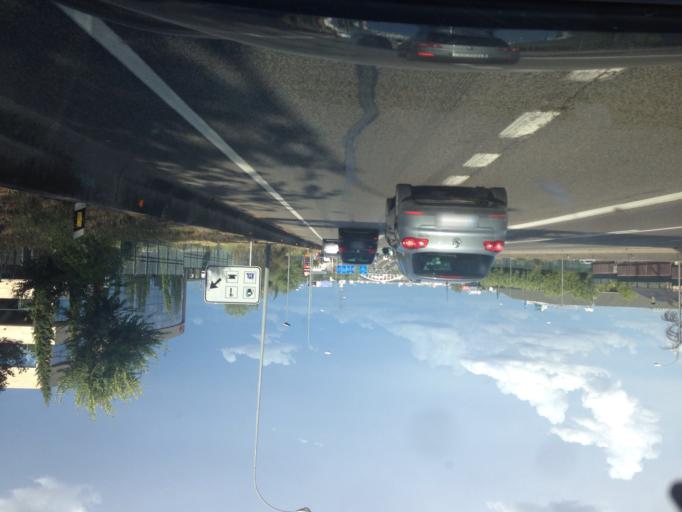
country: ES
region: Madrid
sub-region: Provincia de Madrid
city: Pozuelo de Alarcon
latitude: 40.4661
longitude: -3.8075
